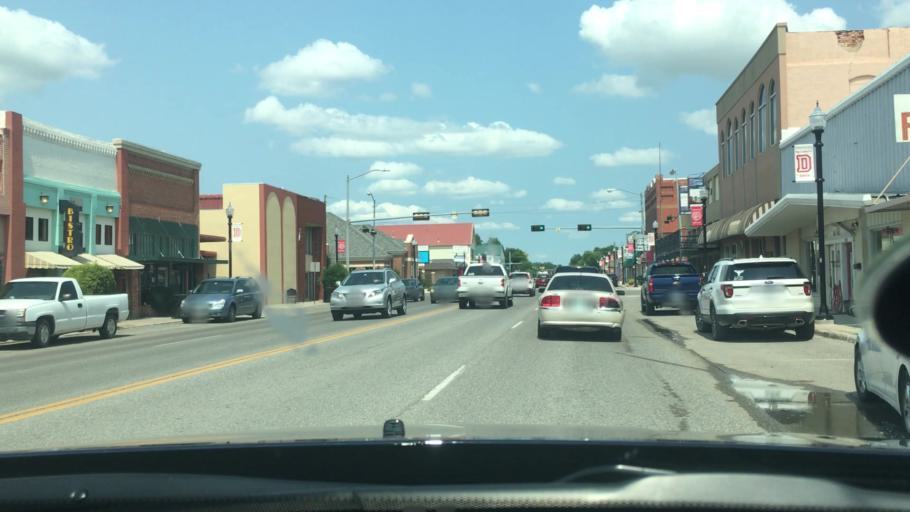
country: US
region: Oklahoma
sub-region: Murray County
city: Davis
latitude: 34.5042
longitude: -97.1204
